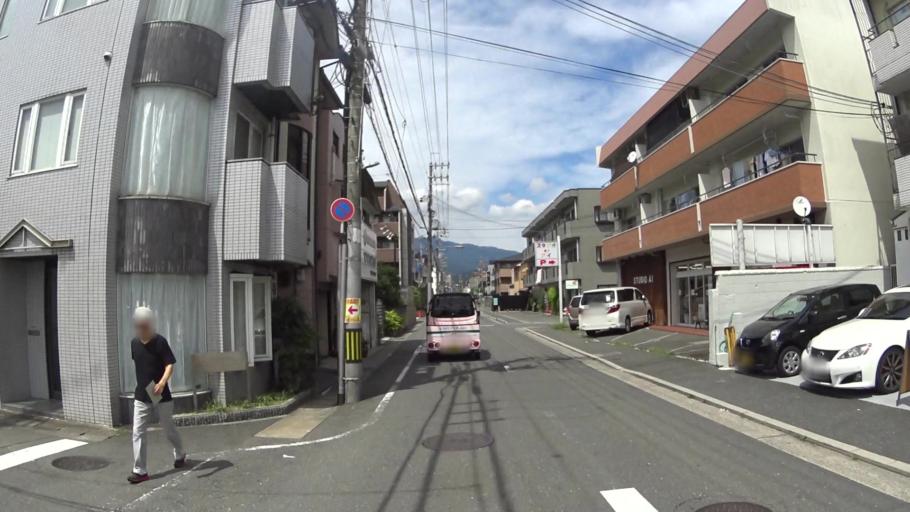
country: JP
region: Kyoto
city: Muko
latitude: 35.0019
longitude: 135.6867
